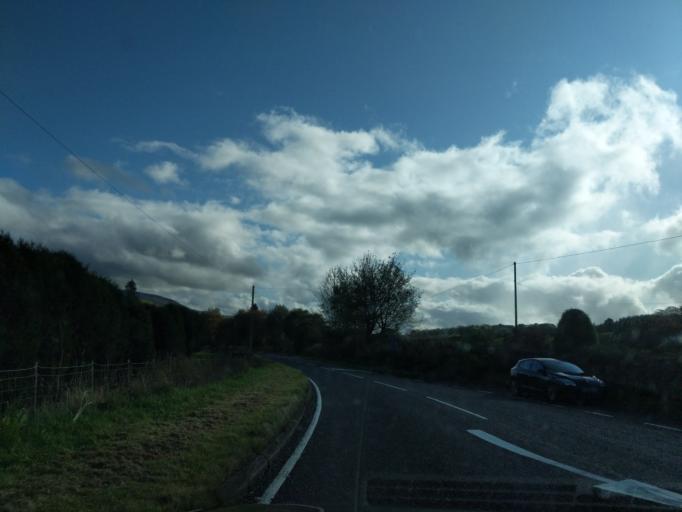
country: GB
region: Scotland
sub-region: Dumfries and Galloway
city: Moffat
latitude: 55.3390
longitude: -3.4571
